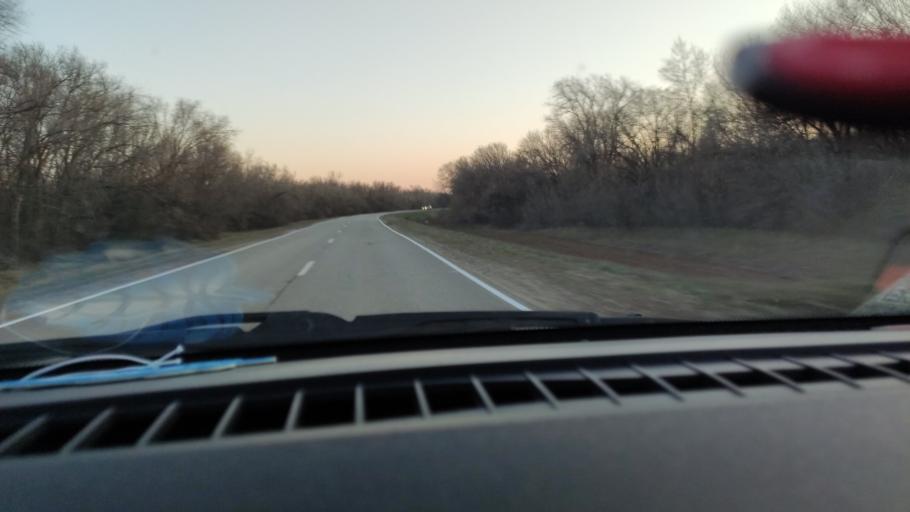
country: RU
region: Saratov
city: Privolzhskiy
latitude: 51.2404
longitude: 45.9291
